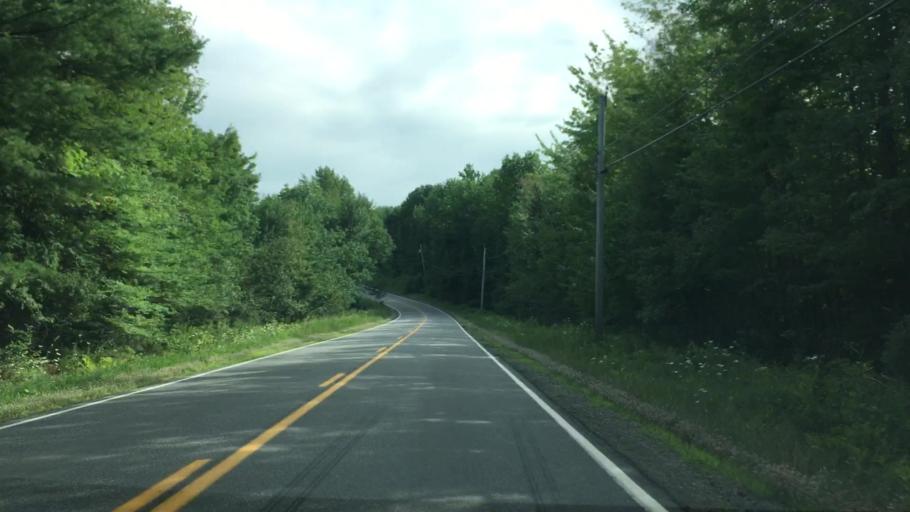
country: US
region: Maine
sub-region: Waldo County
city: Belfast
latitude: 44.3834
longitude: -69.0346
